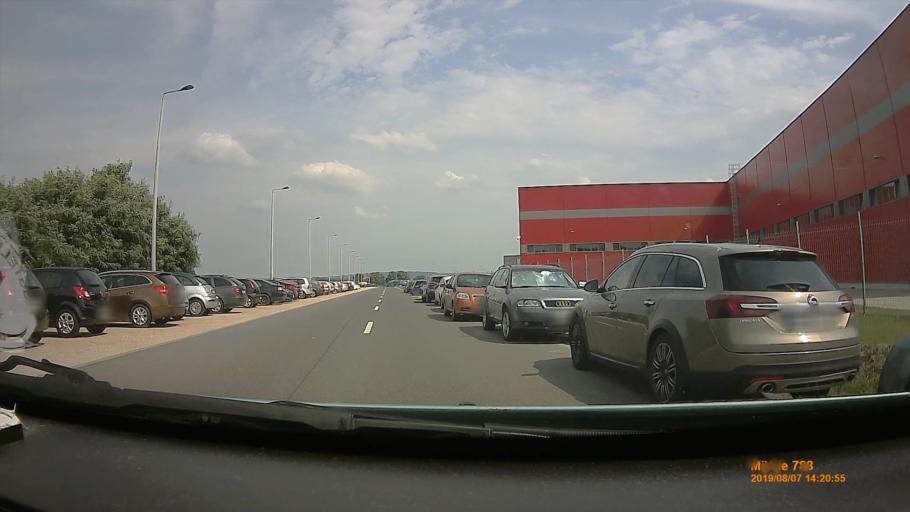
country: HU
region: Borsod-Abauj-Zemplen
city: Szikszo
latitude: 48.1766
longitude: 20.9179
